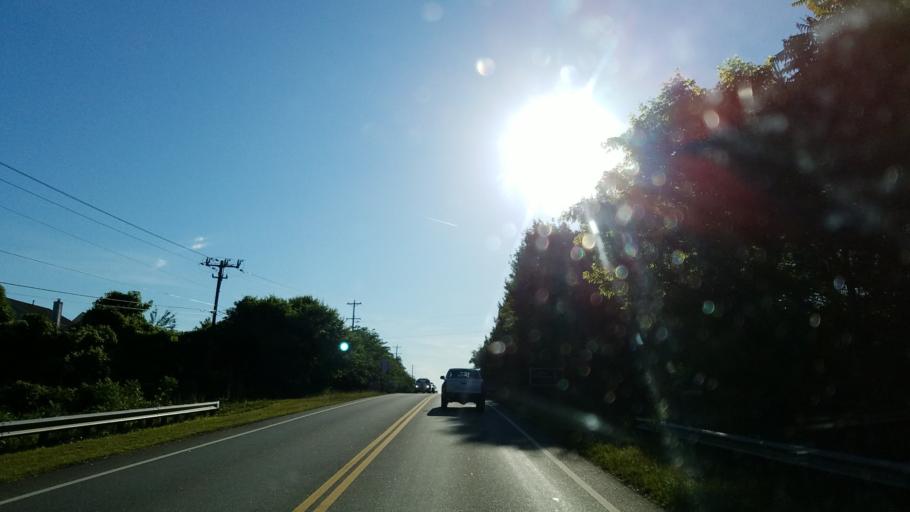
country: US
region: Georgia
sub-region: Cherokee County
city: Holly Springs
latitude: 34.1679
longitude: -84.4395
